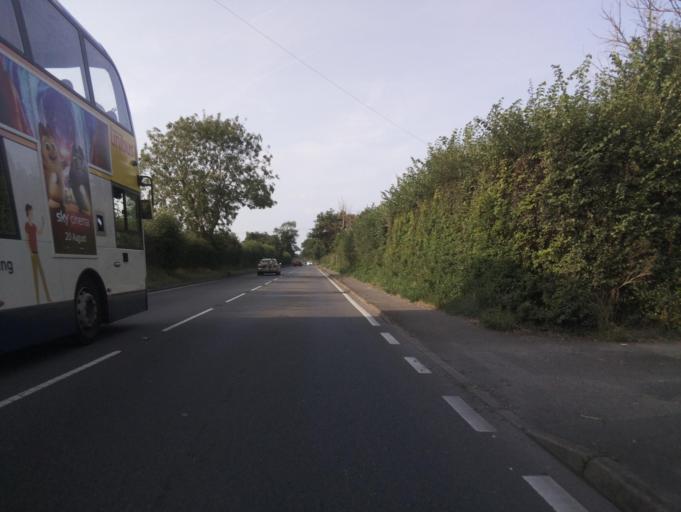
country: GB
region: England
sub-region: Warwickshire
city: Alcester
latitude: 52.2329
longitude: -1.8811
